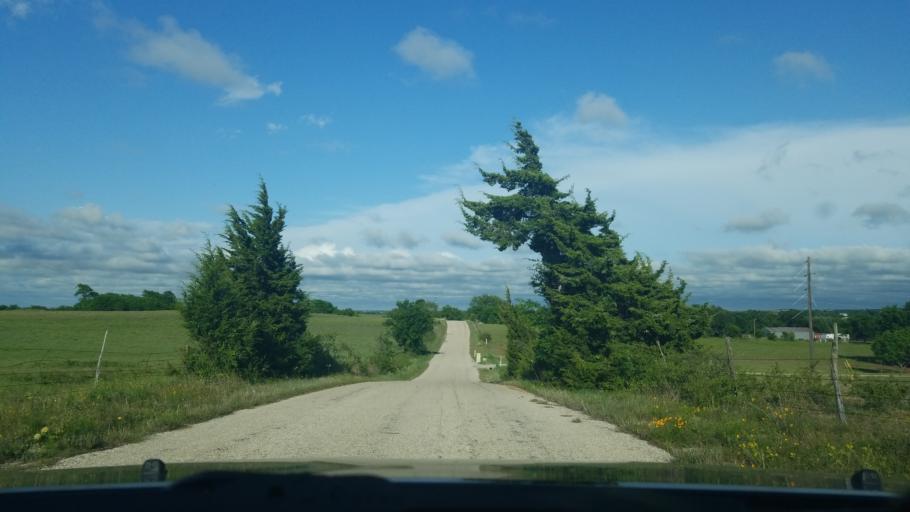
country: US
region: Texas
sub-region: Wise County
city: Decatur
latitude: 33.2428
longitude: -97.4881
